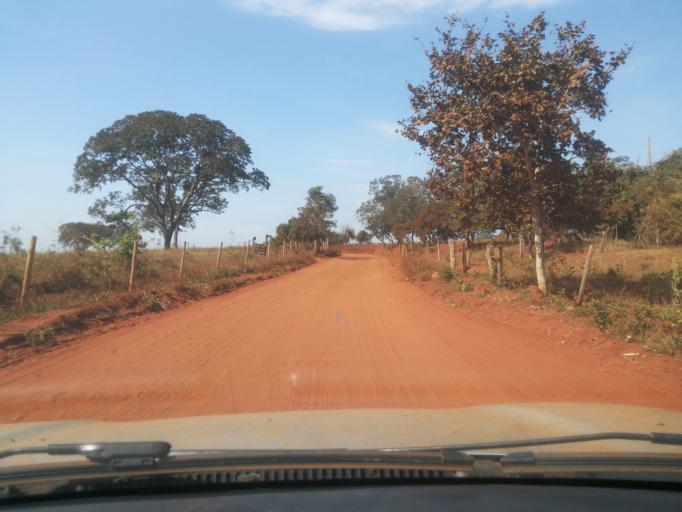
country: BR
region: Minas Gerais
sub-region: Ituiutaba
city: Ituiutaba
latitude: -19.0347
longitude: -49.3858
